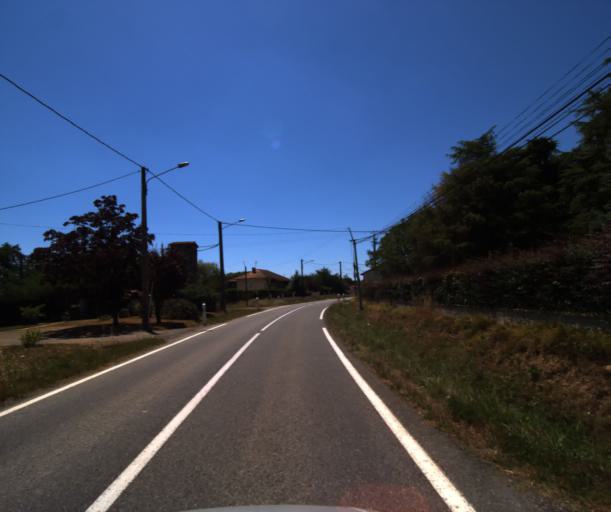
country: FR
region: Midi-Pyrenees
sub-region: Departement de la Haute-Garonne
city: Seysses
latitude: 43.4674
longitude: 1.3016
